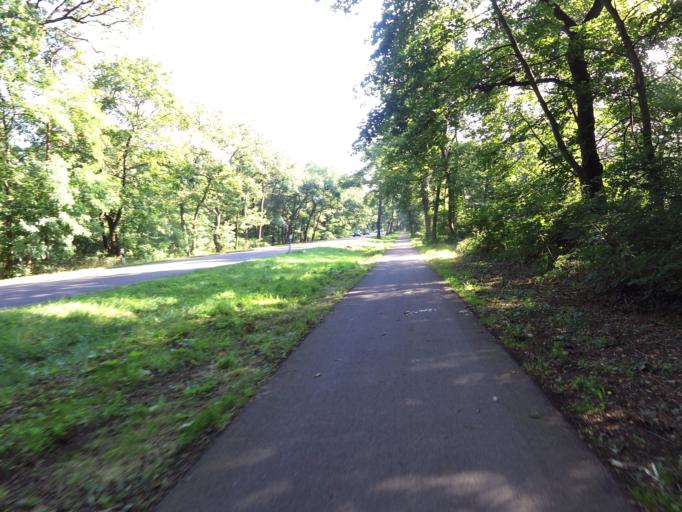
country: DE
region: Saxony-Anhalt
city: Coswig
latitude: 51.8813
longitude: 12.4883
